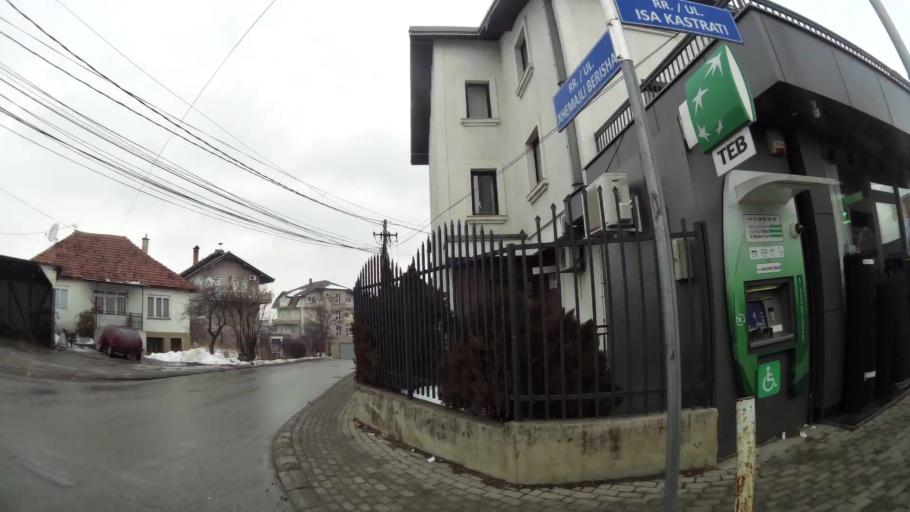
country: XK
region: Pristina
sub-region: Komuna e Prishtines
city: Pristina
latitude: 42.6592
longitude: 21.1778
